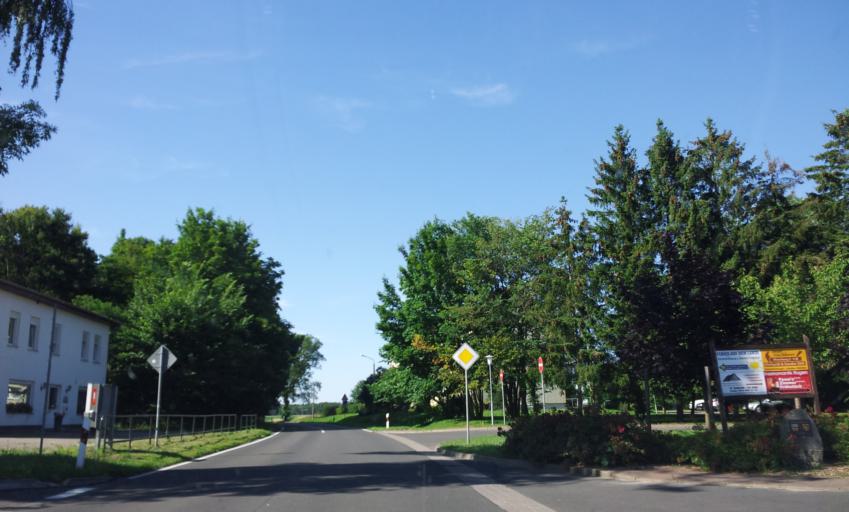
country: DE
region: Mecklenburg-Vorpommern
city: Samtens
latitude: 54.4036
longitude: 13.2922
